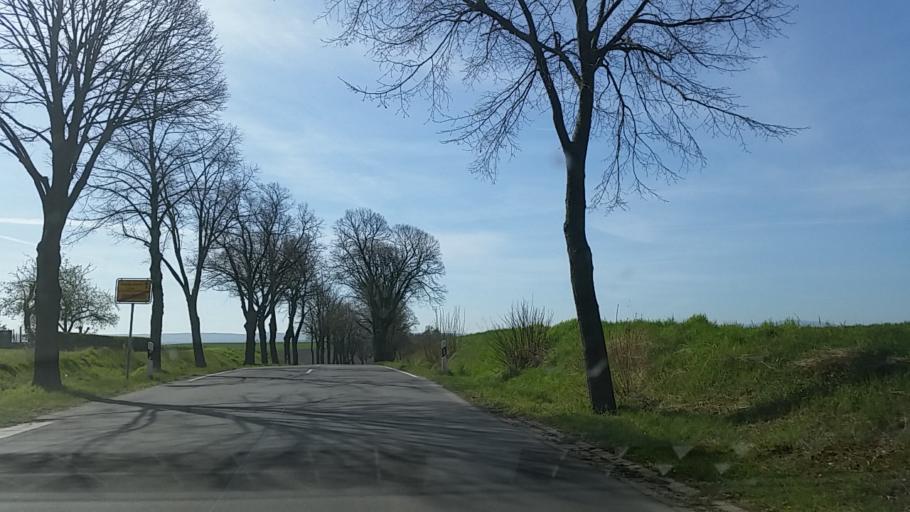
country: DE
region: Lower Saxony
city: Jerxheim
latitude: 52.0815
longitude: 10.8945
